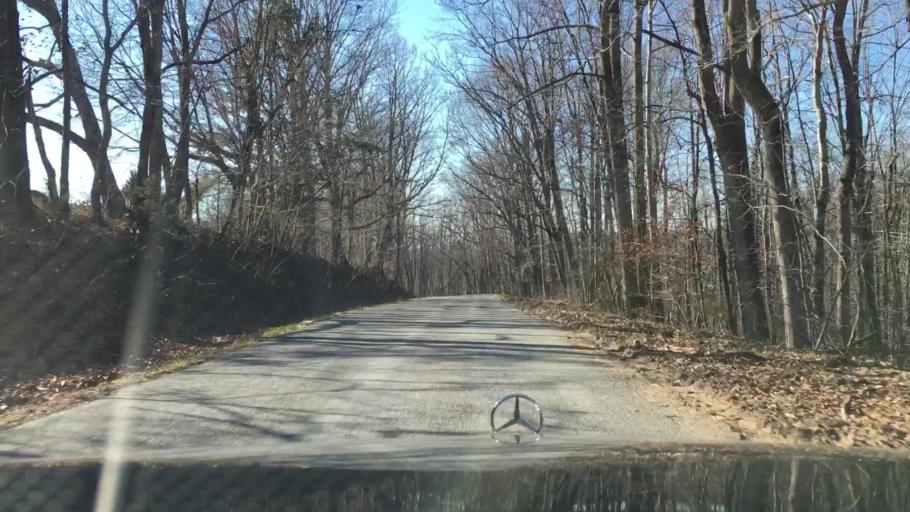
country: US
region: Virginia
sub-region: Campbell County
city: Altavista
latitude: 37.1669
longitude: -79.3529
